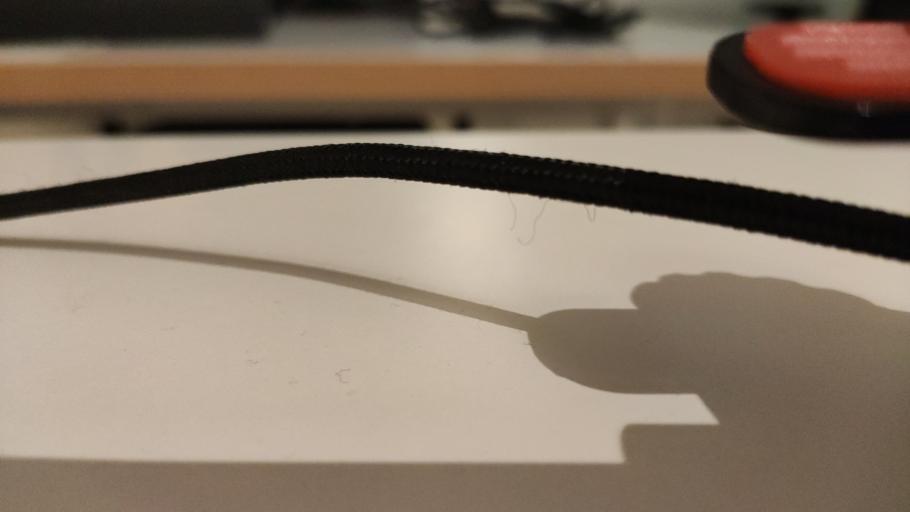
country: RU
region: Moskovskaya
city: Shaburnovo
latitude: 56.4212
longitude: 37.9760
